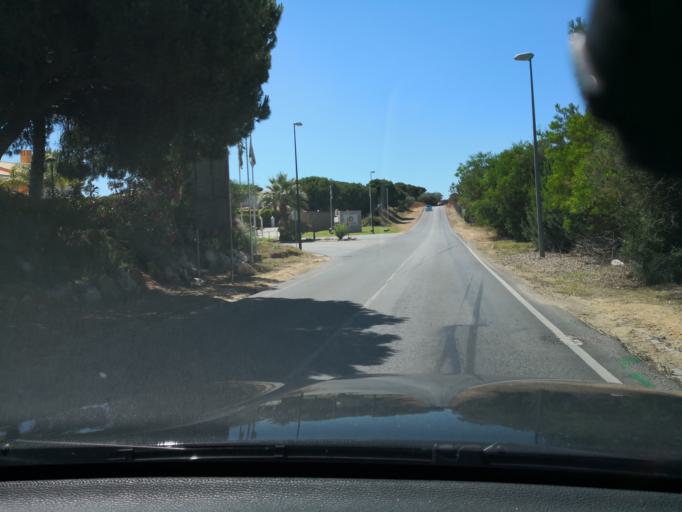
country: PT
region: Faro
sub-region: Loule
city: Vilamoura
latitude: 37.0912
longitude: -8.1025
